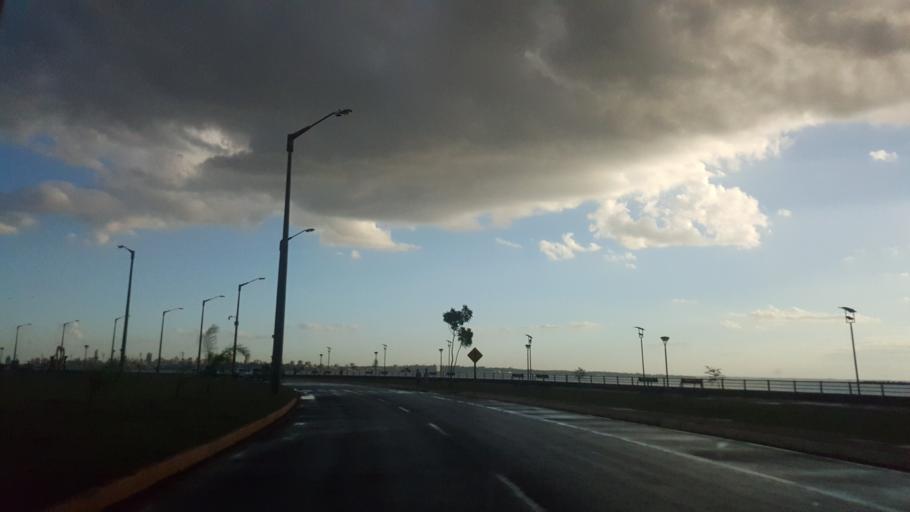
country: PY
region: Itapua
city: Encarnacion
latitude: -27.3217
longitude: -55.8754
